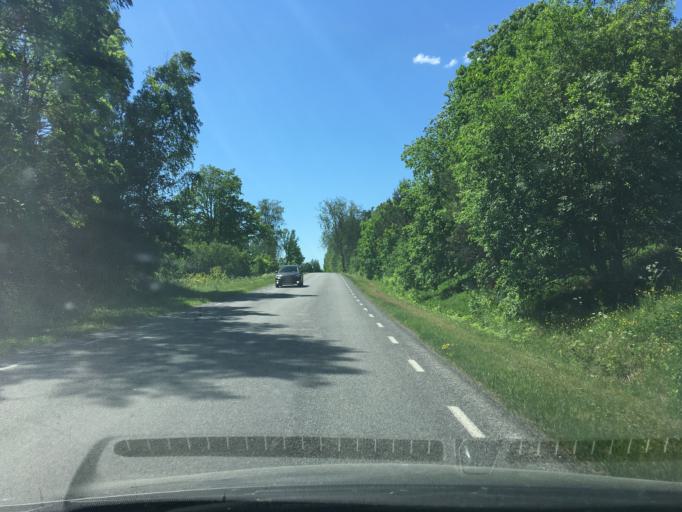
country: EE
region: Raplamaa
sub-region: Kohila vald
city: Kohila
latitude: 59.1011
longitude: 24.8139
